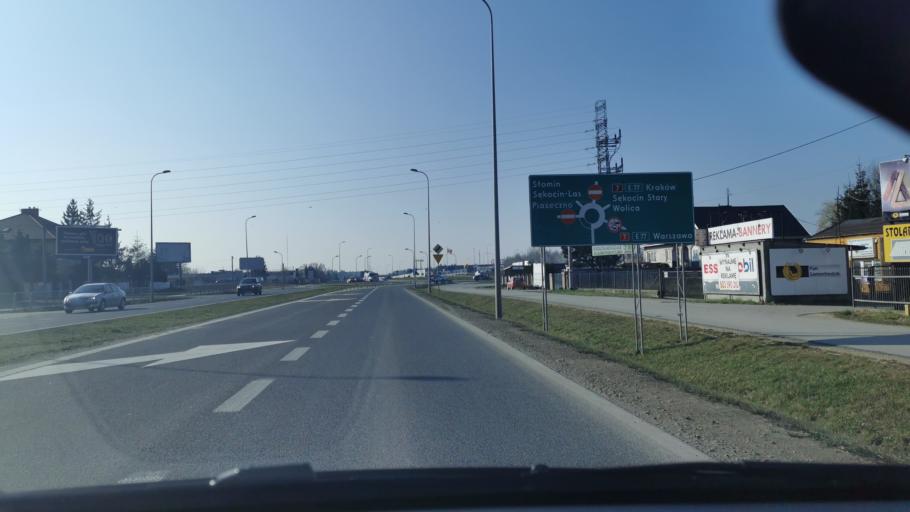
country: PL
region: Masovian Voivodeship
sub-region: Powiat pruszkowski
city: Nowe Grocholice
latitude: 52.1156
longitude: 20.8913
